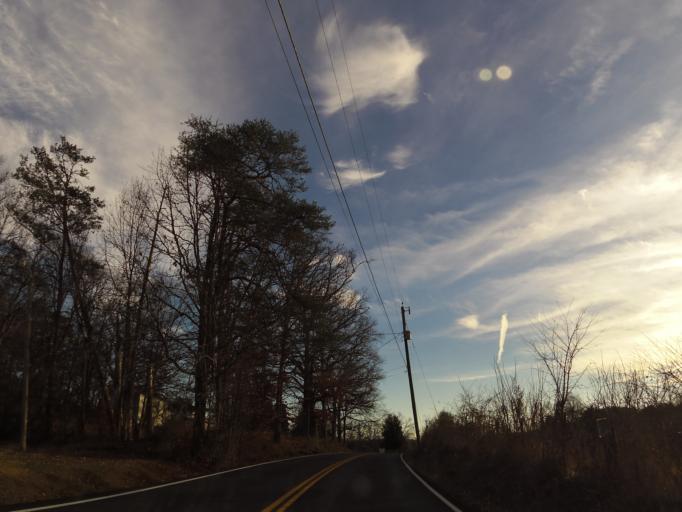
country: US
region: Tennessee
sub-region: Knox County
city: Mascot
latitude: 35.9886
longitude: -83.6958
